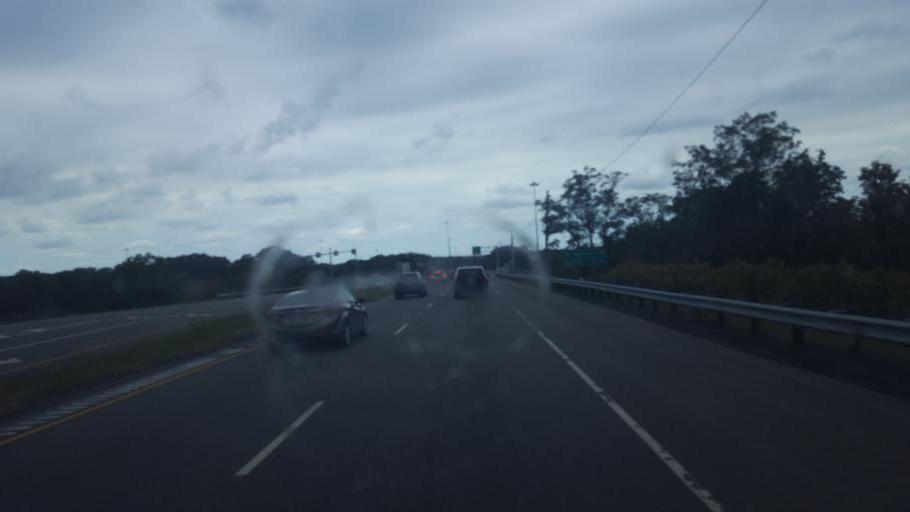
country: US
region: Ohio
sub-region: Lake County
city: Painesville
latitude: 41.6673
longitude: -81.2450
